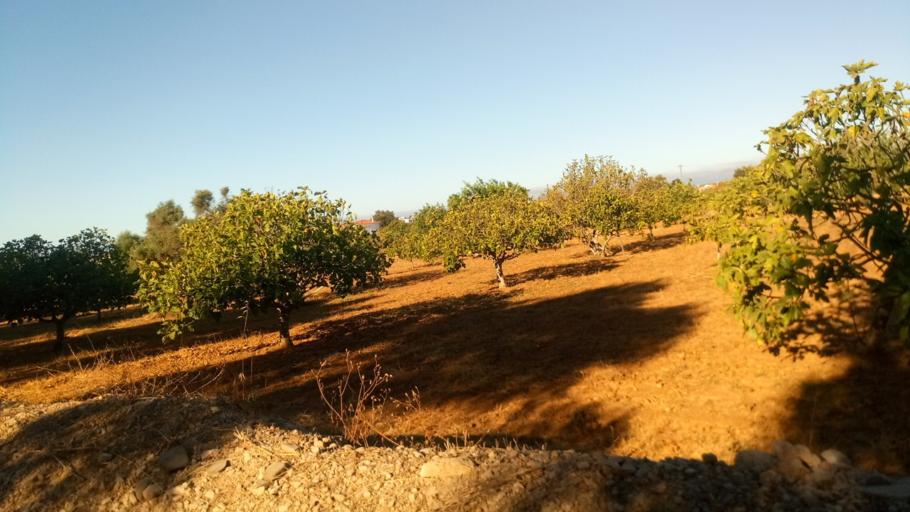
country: PT
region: Faro
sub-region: Tavira
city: Tavira
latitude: 37.1439
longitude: -7.5940
